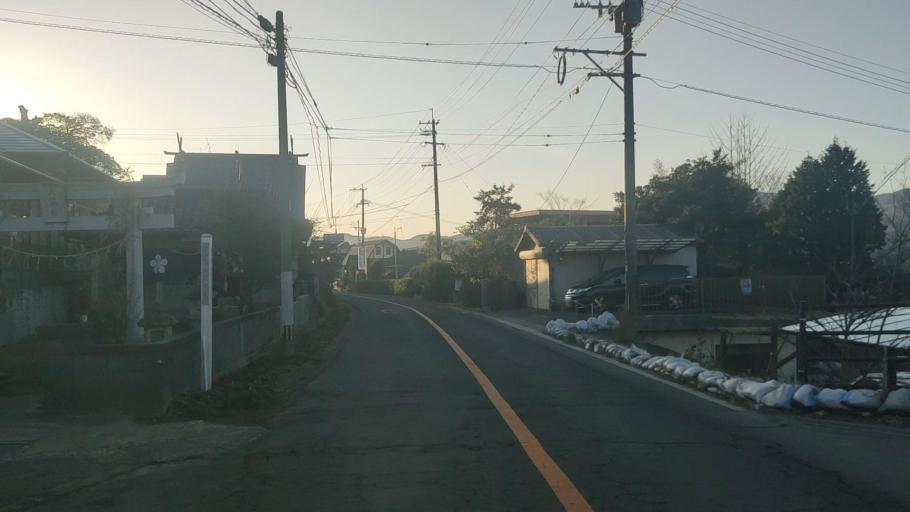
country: JP
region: Oita
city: Beppu
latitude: 33.2551
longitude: 131.3602
